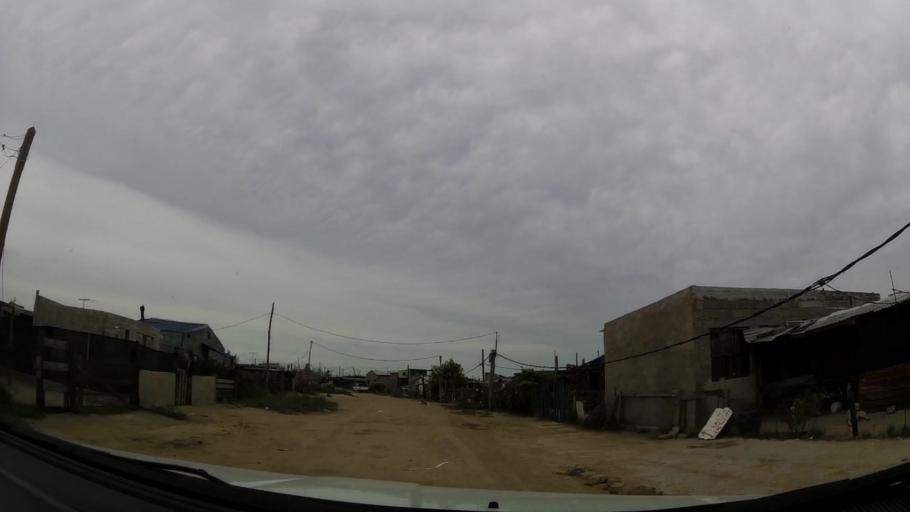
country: UY
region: Maldonado
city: Maldonado
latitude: -34.8859
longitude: -54.9570
